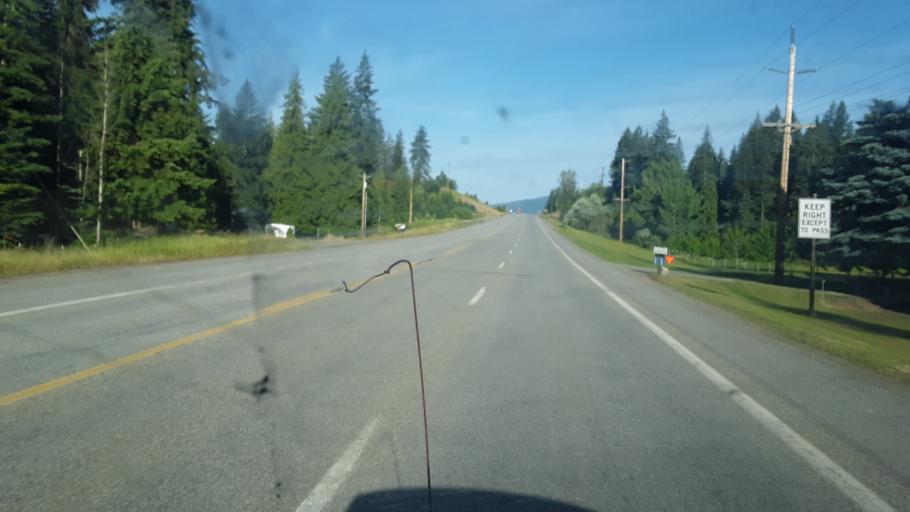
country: US
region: Idaho
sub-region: Boundary County
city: Bonners Ferry
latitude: 48.7317
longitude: -116.2495
